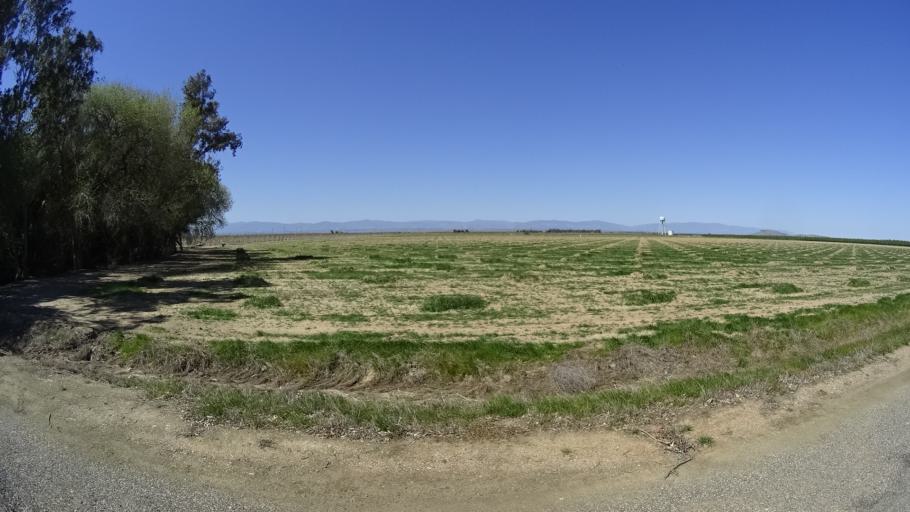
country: US
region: California
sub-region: Glenn County
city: Orland
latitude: 39.6781
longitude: -122.2343
